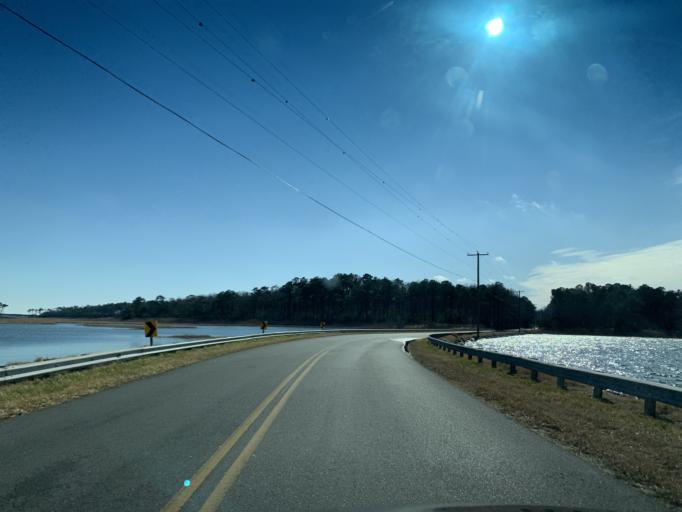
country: US
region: Maryland
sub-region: Worcester County
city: Ocean Pines
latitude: 38.3999
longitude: -75.1085
